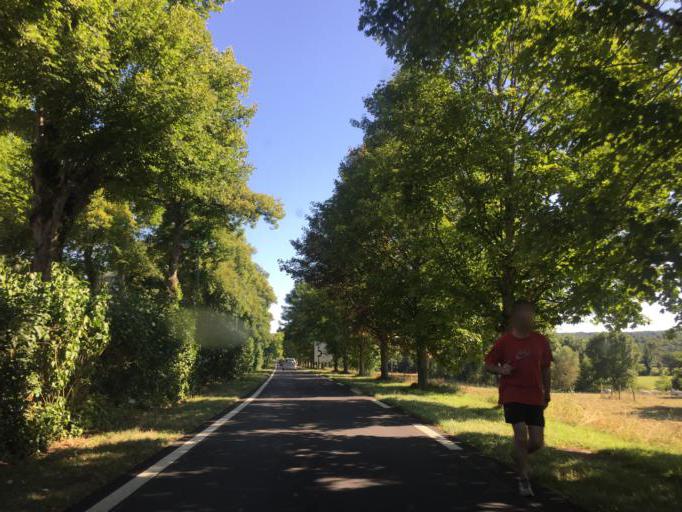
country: FR
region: Bourgogne
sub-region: Departement de la Nievre
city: Clamecy
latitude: 47.4558
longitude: 3.5503
